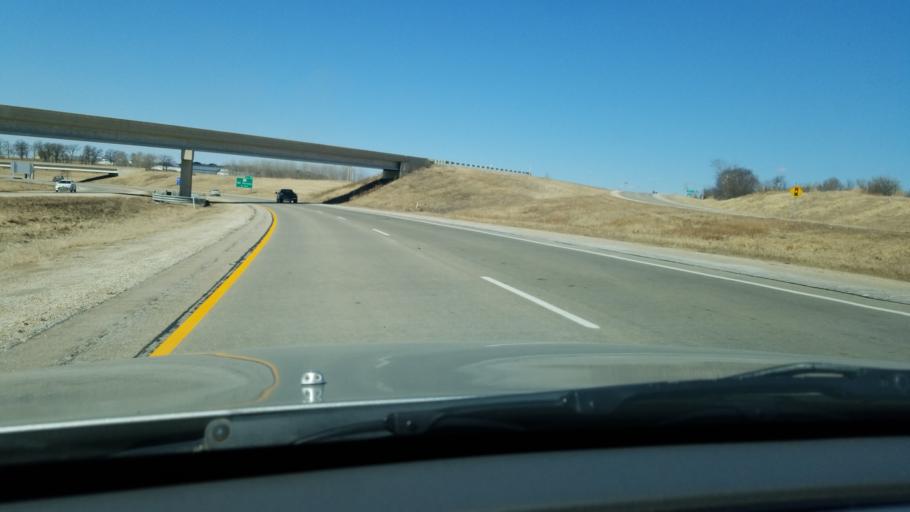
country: US
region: Wisconsin
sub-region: Dane County
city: Verona
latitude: 42.9840
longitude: -89.5580
